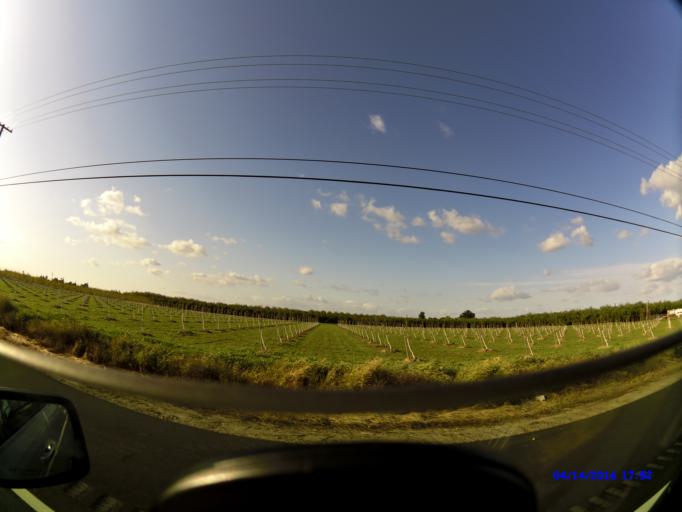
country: US
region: California
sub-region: Stanislaus County
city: Del Rio
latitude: 37.7111
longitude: -120.9869
